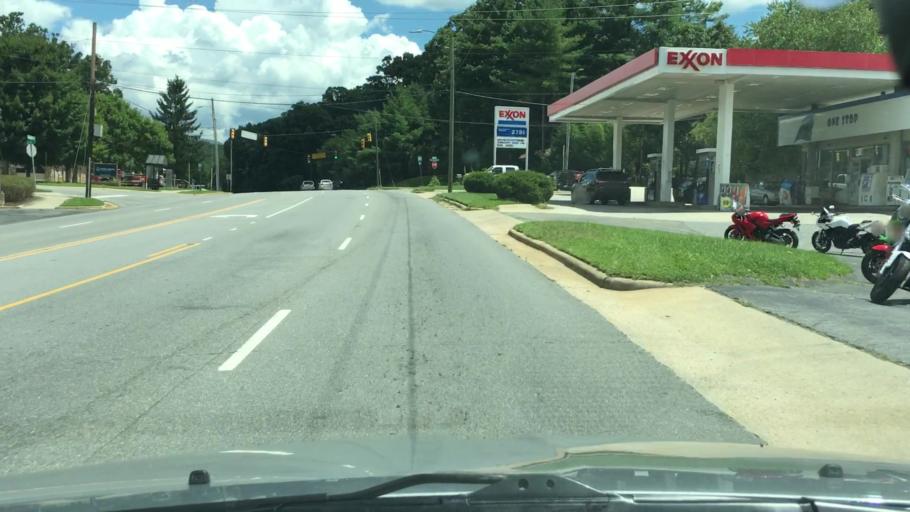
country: US
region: North Carolina
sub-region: Buncombe County
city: Asheville
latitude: 35.5869
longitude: -82.5038
